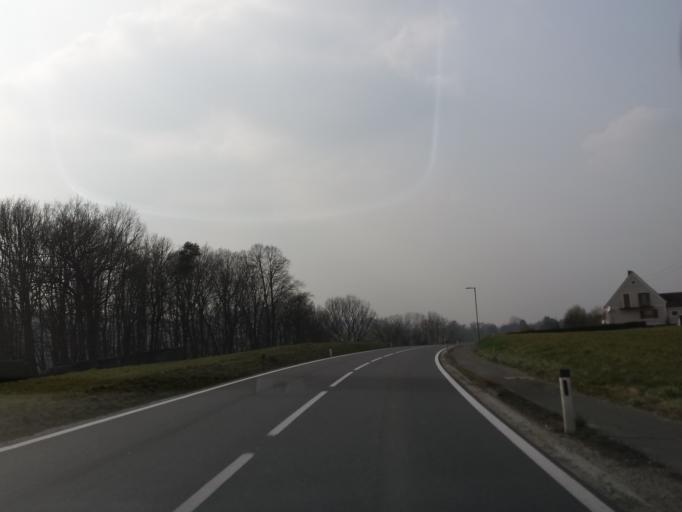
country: AT
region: Styria
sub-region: Politischer Bezirk Suedoststeiermark
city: Breitenfeld an der Rittschein
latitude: 47.0734
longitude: 15.9788
